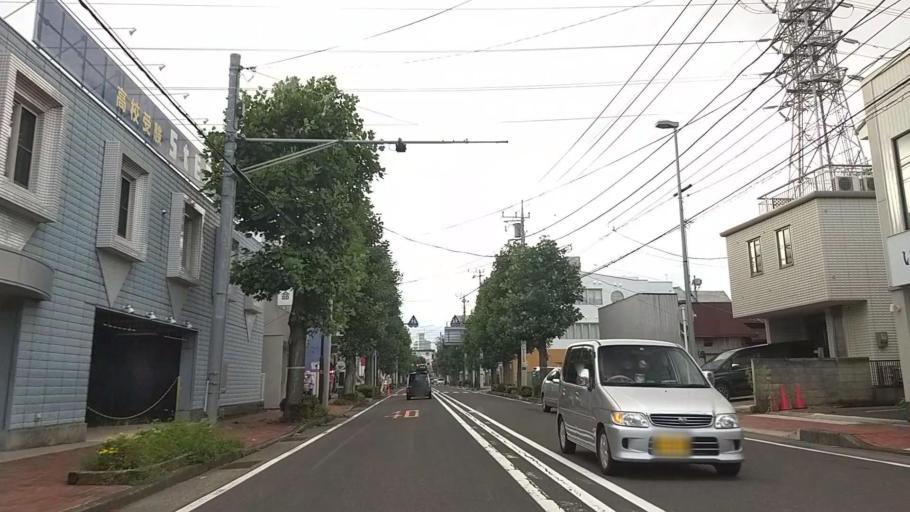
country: JP
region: Kanagawa
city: Isehara
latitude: 35.3928
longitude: 139.3144
